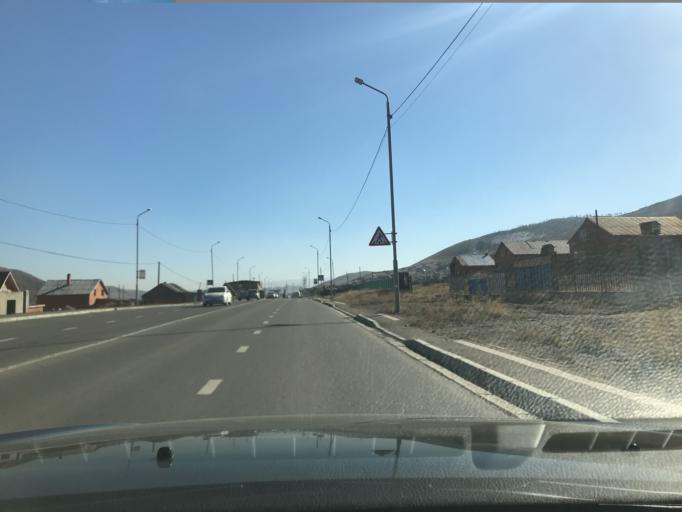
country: MN
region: Ulaanbaatar
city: Ulaanbaatar
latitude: 48.0400
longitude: 106.9047
